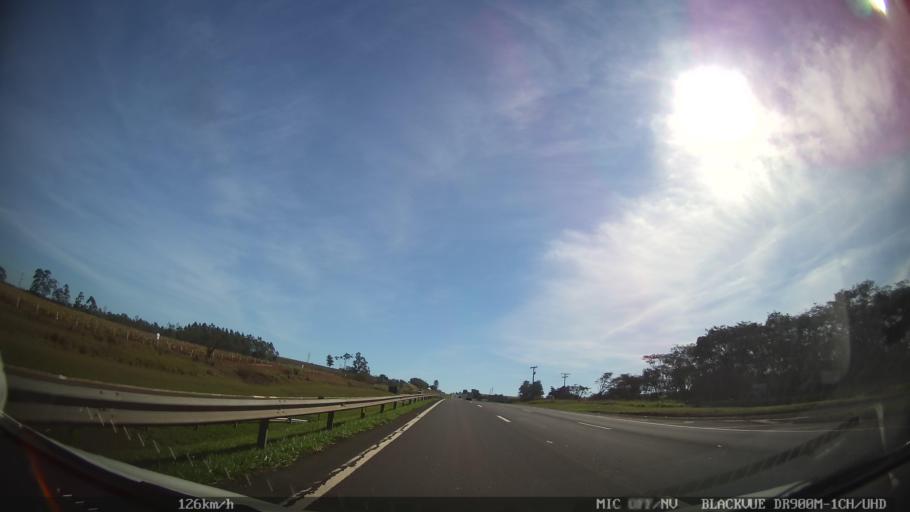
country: BR
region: Sao Paulo
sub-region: Leme
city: Leme
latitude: -22.0944
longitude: -47.4172
